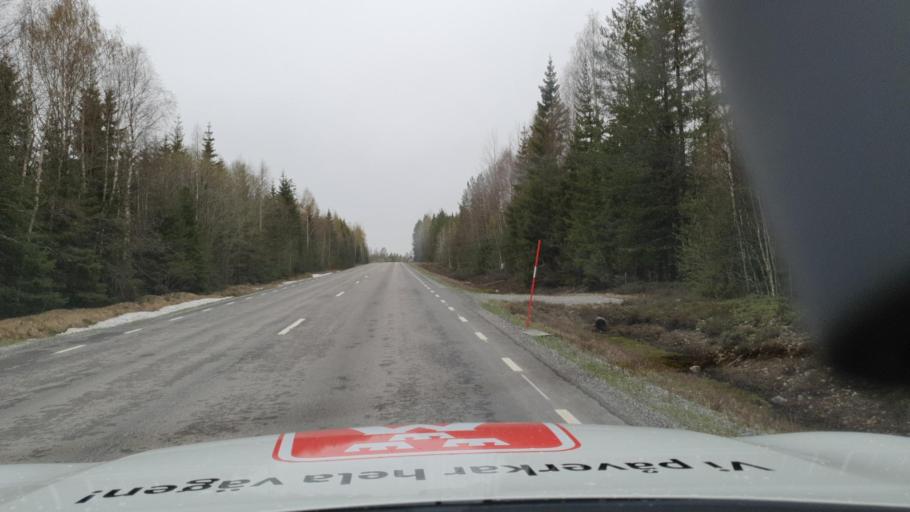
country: SE
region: Vaesterbotten
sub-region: Umea Kommun
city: Hoernefors
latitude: 63.7771
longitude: 19.8885
